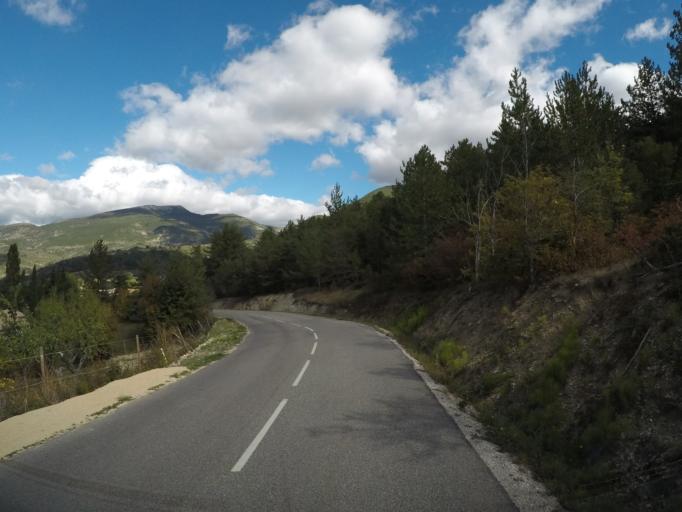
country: FR
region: Provence-Alpes-Cote d'Azur
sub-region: Departement du Vaucluse
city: Sault
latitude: 44.1663
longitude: 5.4470
